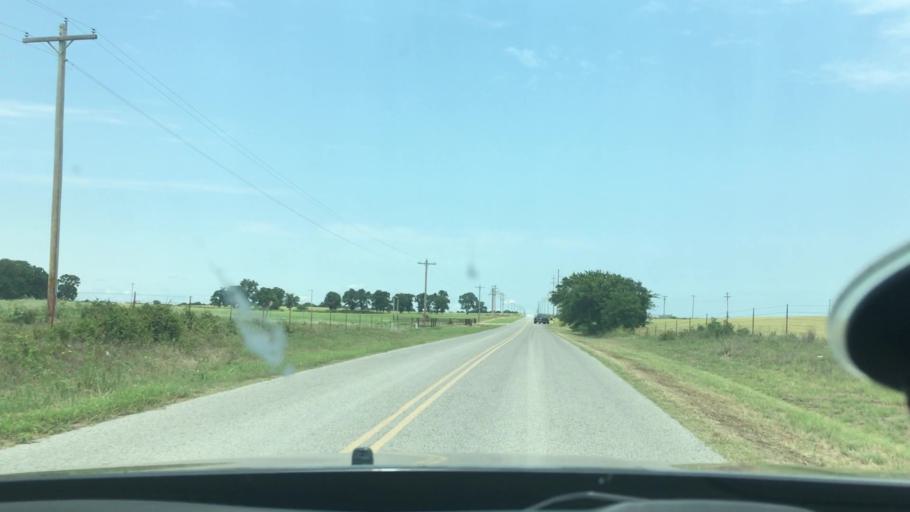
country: US
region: Oklahoma
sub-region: Love County
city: Marietta
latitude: 33.9077
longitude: -97.3521
